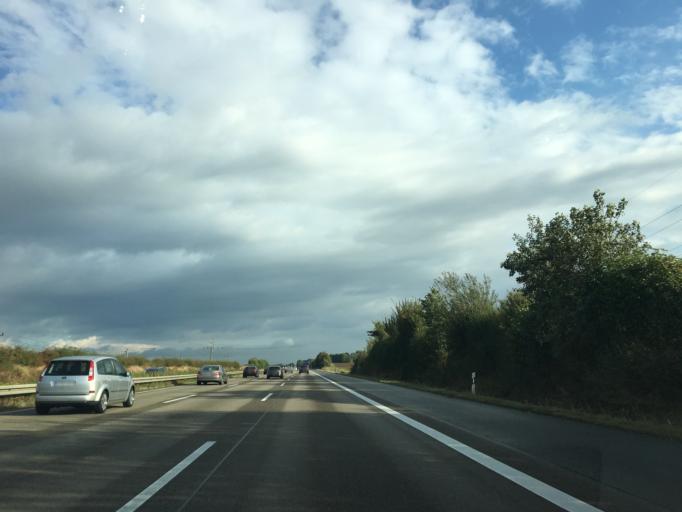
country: DE
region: Hesse
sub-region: Regierungsbezirk Giessen
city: Steeden
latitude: 50.3649
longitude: 8.1246
